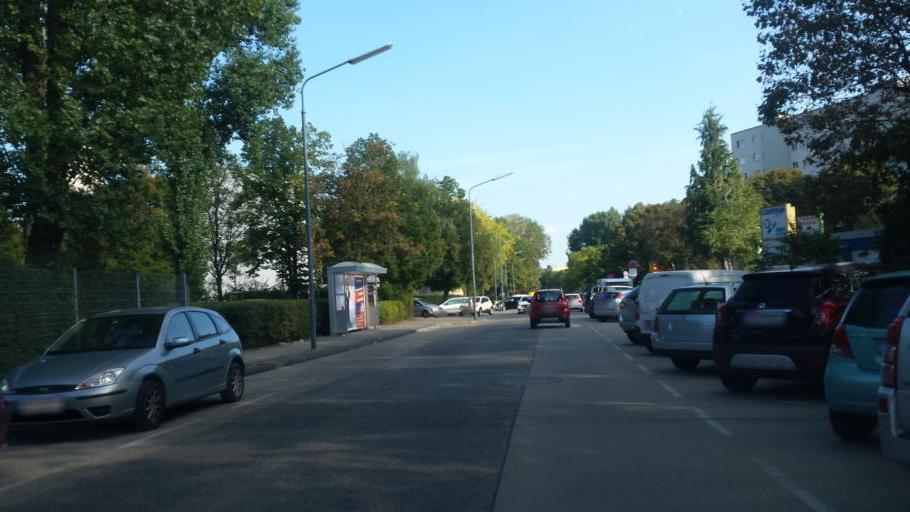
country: AT
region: Lower Austria
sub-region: Politischer Bezirk Wien-Umgebung
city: Leopoldsdorf
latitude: 48.1491
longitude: 16.3854
